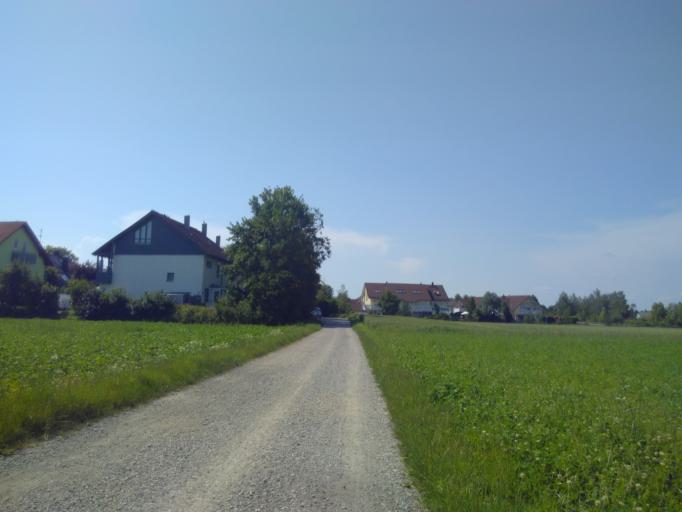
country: DE
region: Bavaria
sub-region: Upper Bavaria
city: Olching
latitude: 48.2015
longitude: 11.3399
